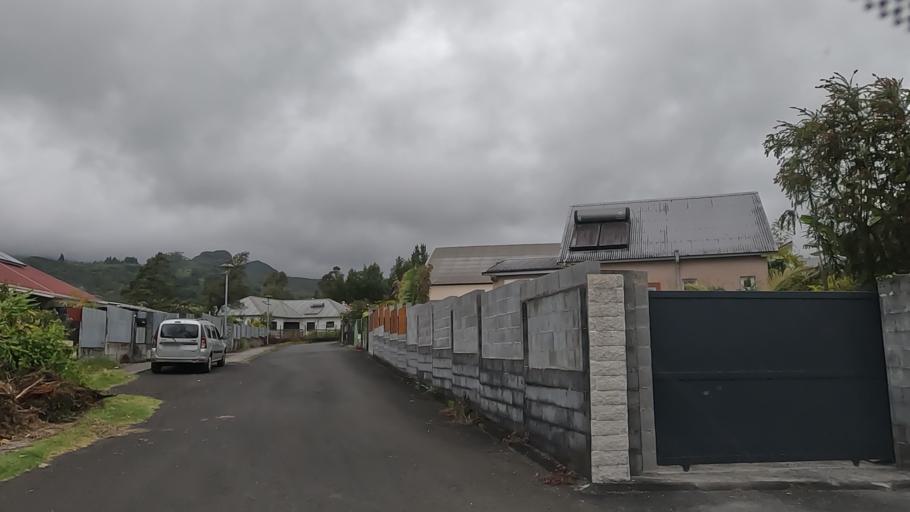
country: RE
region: Reunion
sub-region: Reunion
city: Saint-Benoit
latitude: -21.1386
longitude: 55.6271
